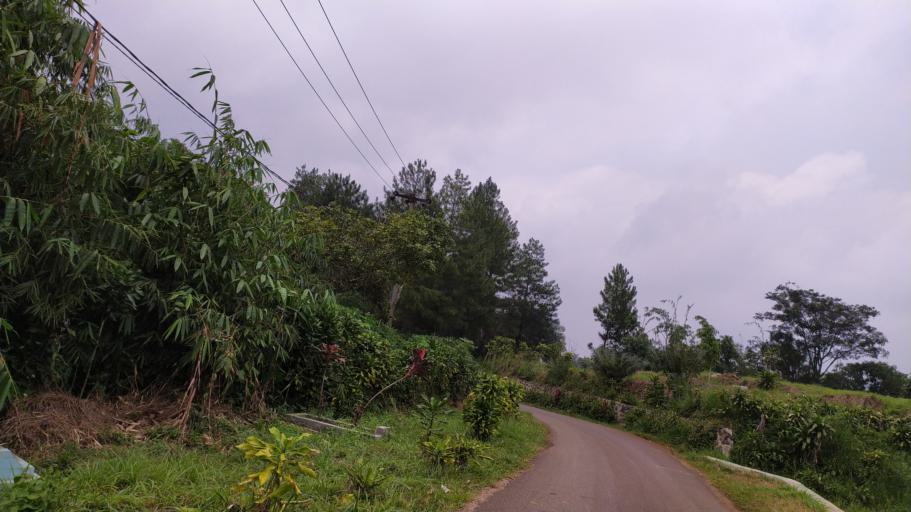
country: ID
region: West Java
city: Ciampea
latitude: -6.6285
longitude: 106.7074
